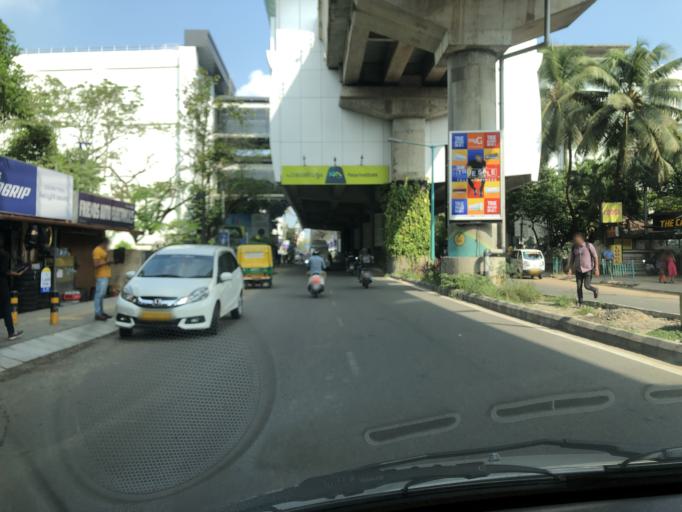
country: IN
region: Kerala
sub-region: Ernakulam
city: Elur
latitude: 10.0057
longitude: 76.3049
